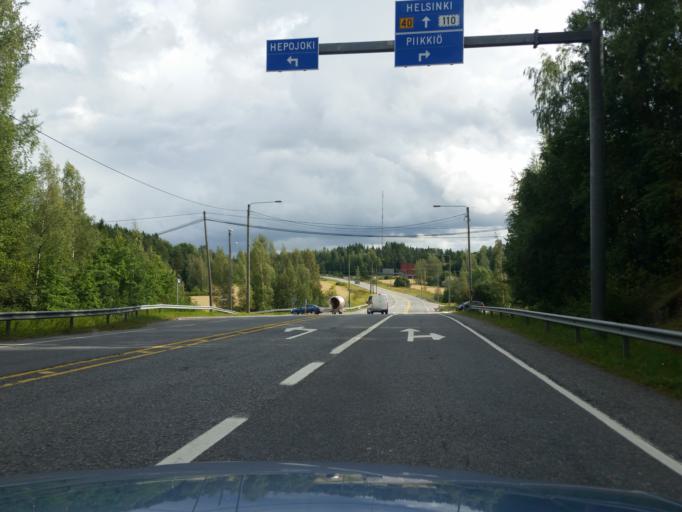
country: FI
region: Varsinais-Suomi
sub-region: Turku
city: Piikkioe
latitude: 60.4344
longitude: 22.5244
